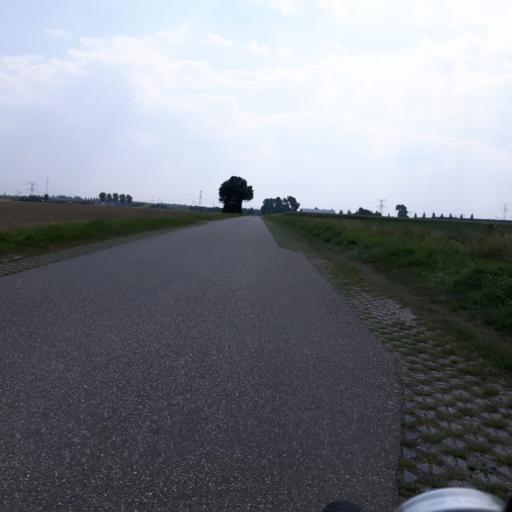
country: NL
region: Zeeland
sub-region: Gemeente Reimerswaal
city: Yerseke
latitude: 51.4780
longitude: 3.9861
